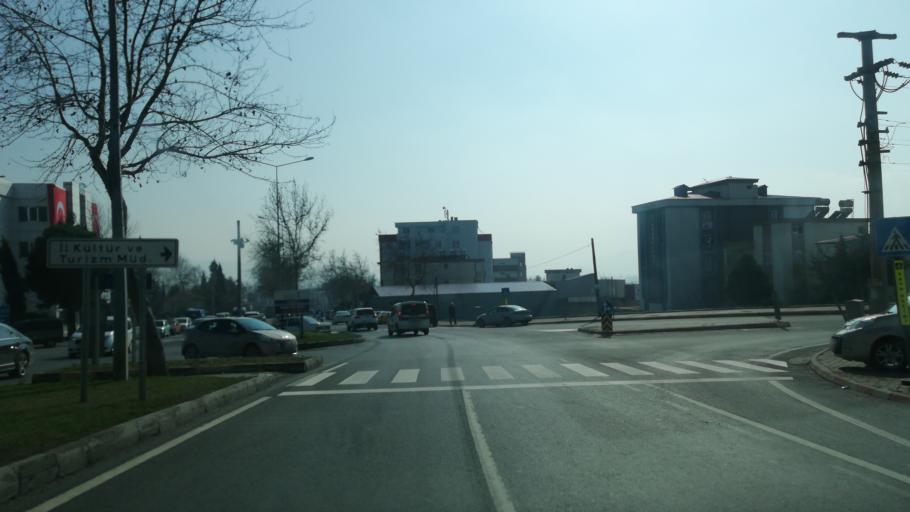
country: TR
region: Kahramanmaras
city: Kahramanmaras
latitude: 37.5682
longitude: 36.9423
